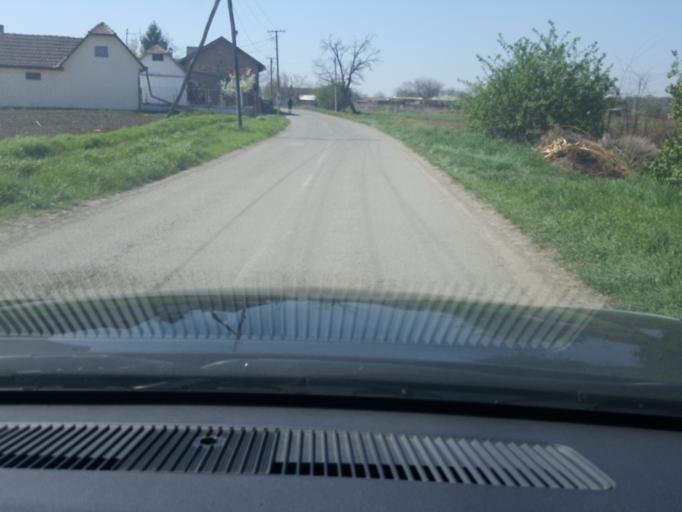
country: RS
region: Autonomna Pokrajina Vojvodina
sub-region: Zapadnobacki Okrug
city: Sombor
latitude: 45.7704
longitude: 19.0861
